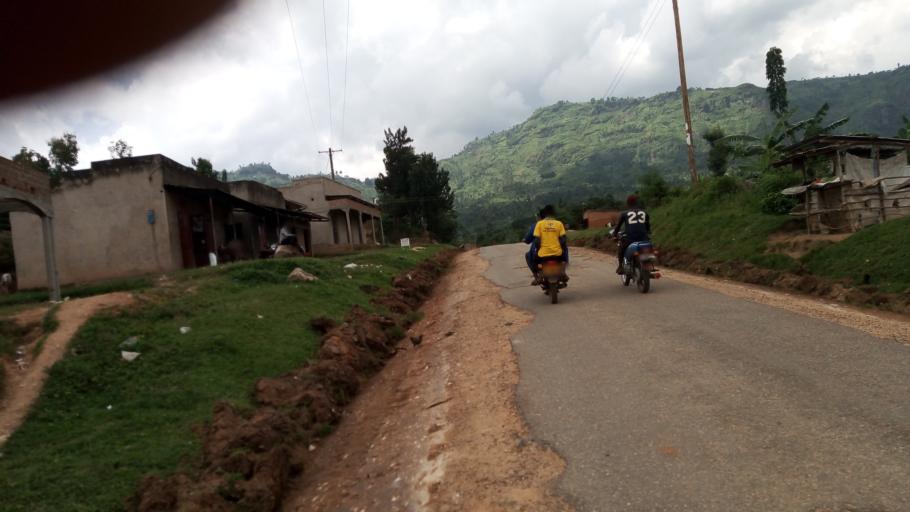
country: UG
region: Eastern Region
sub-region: Mbale District
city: Mbale
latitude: 1.0692
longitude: 34.2179
